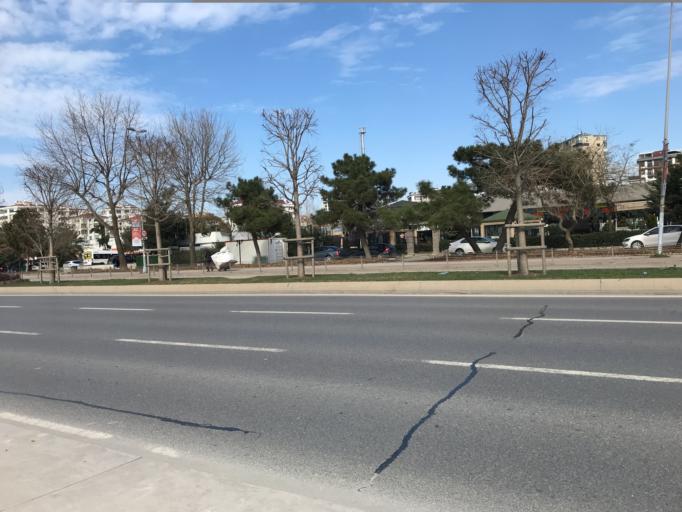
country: TR
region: Istanbul
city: Maltepe
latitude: 40.9244
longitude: 29.1244
